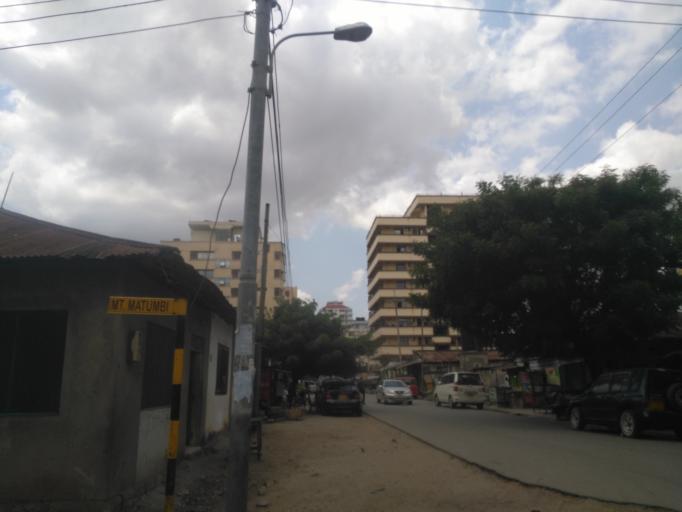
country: TZ
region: Dar es Salaam
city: Dar es Salaam
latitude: -6.8140
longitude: 39.2716
